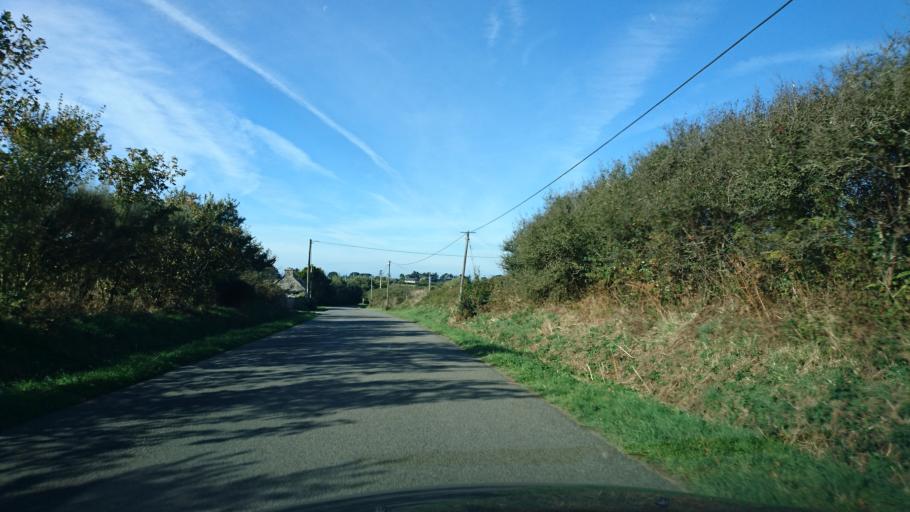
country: FR
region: Brittany
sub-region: Departement du Finistere
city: Lampaul-Plouarzel
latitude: 48.4295
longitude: -4.7585
